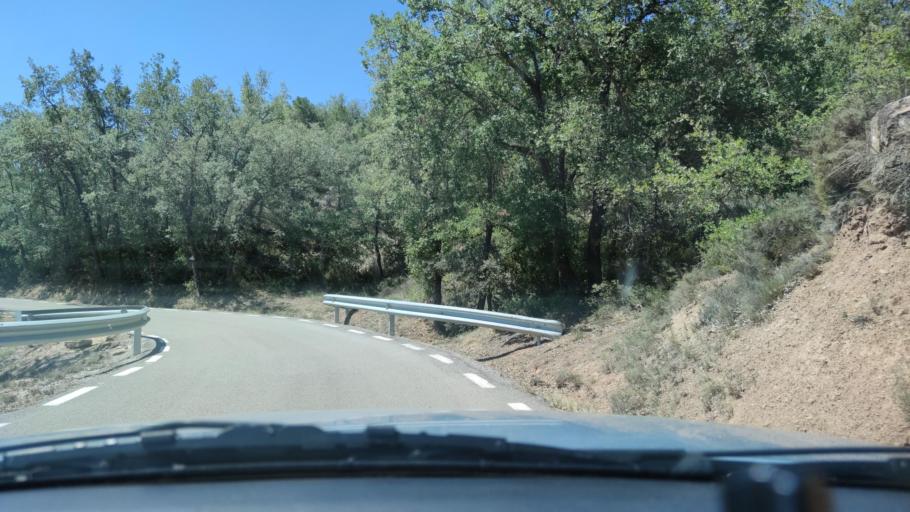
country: ES
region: Catalonia
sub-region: Provincia de Lleida
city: Tora de Riubregos
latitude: 41.8432
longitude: 1.4240
